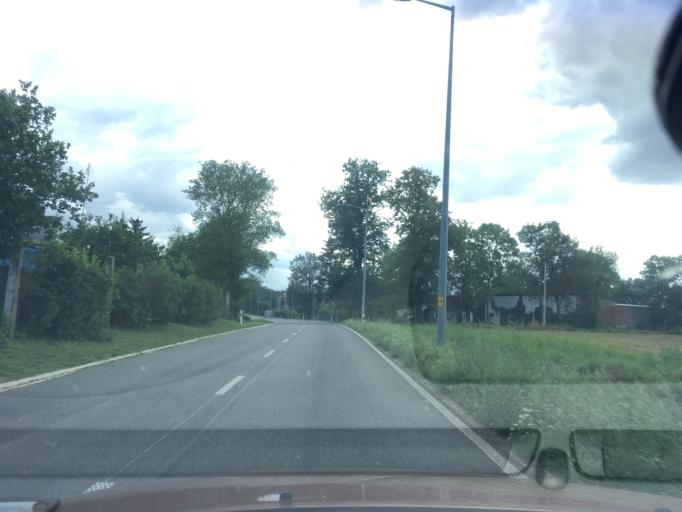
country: PL
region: Lower Silesian Voivodeship
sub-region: Powiat zgorzelecki
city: Piensk
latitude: 51.2264
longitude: 15.0276
